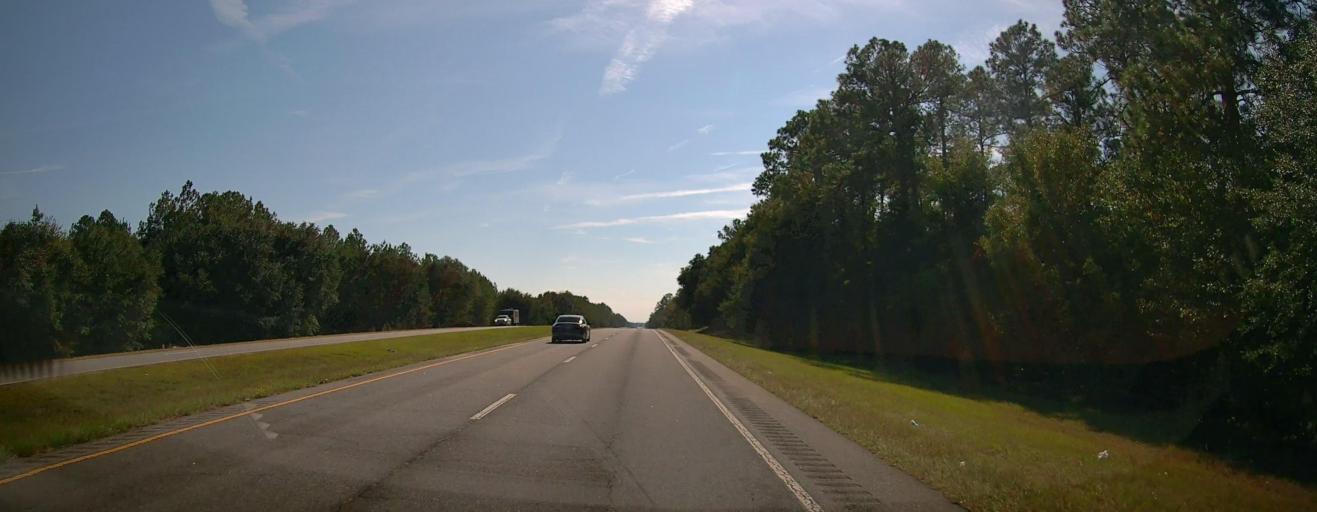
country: US
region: Georgia
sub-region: Lee County
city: Leesburg
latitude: 31.6963
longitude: -83.9921
